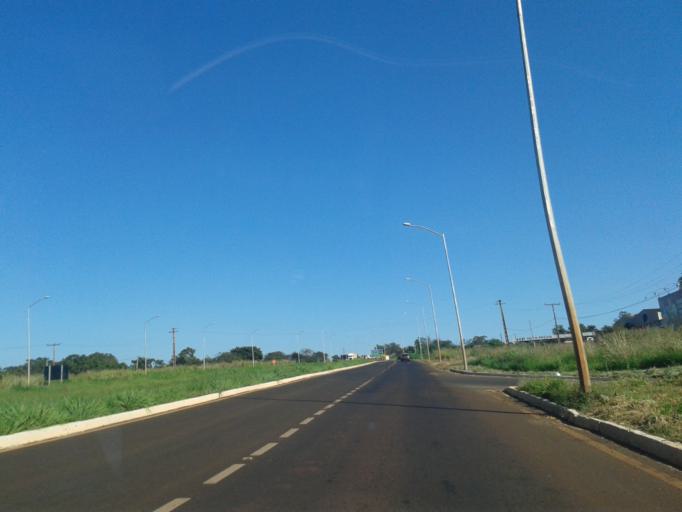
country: BR
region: Minas Gerais
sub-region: Ituiutaba
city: Ituiutaba
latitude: -18.9659
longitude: -49.4906
